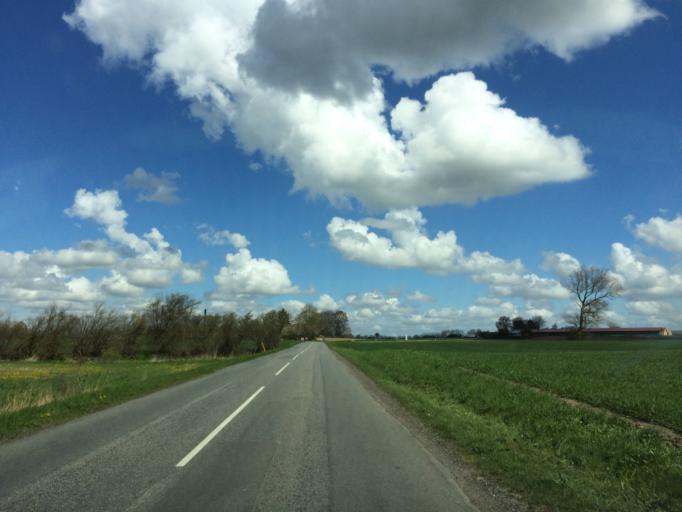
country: DK
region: South Denmark
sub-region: Odense Kommune
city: Bellinge
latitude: 55.2614
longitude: 10.2900
